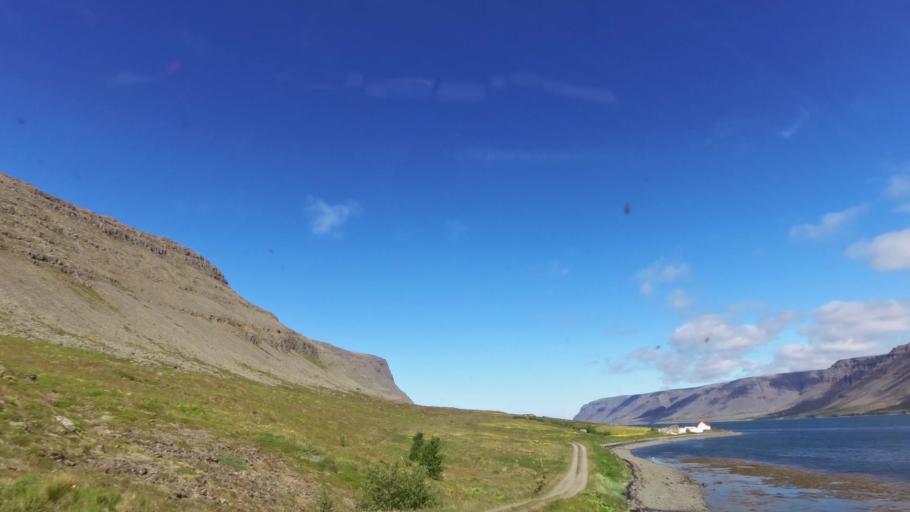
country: IS
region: West
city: Olafsvik
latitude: 65.6185
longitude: -23.8641
